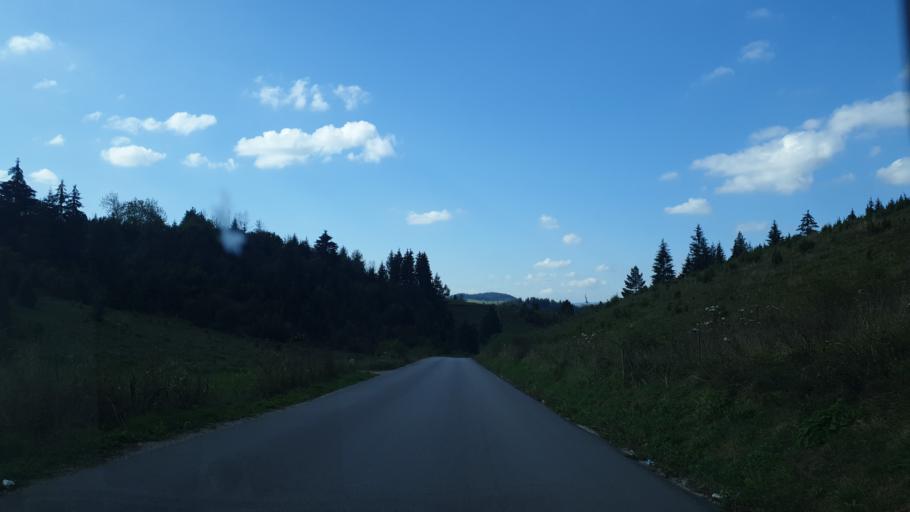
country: RS
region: Central Serbia
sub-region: Zlatiborski Okrug
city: Nova Varos
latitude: 43.4278
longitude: 19.8743
